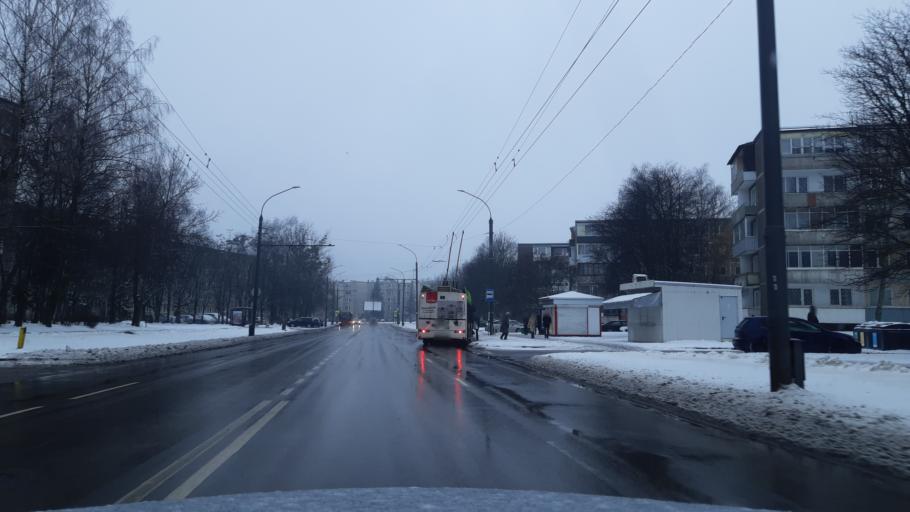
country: LT
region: Kauno apskritis
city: Dainava (Kaunas)
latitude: 54.9152
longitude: 23.9603
